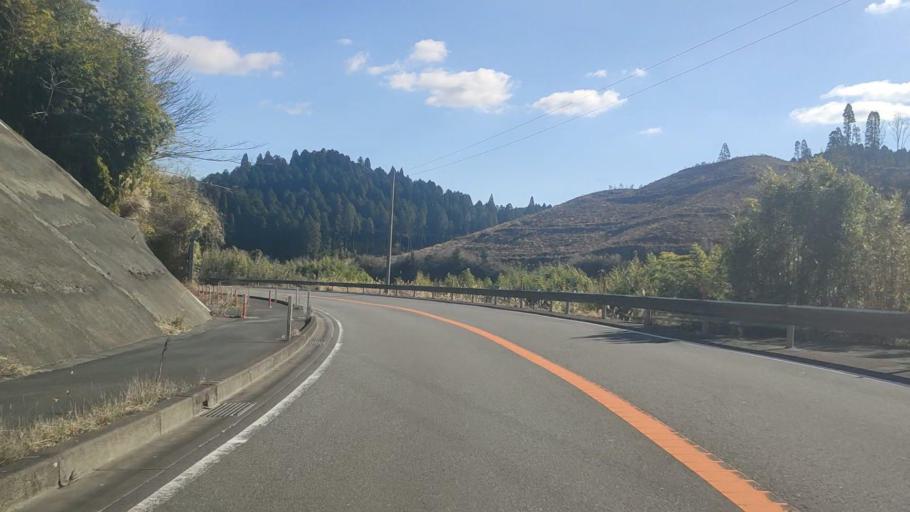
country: JP
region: Kagoshima
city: Sueyoshicho-ninokata
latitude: 31.6610
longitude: 130.8953
